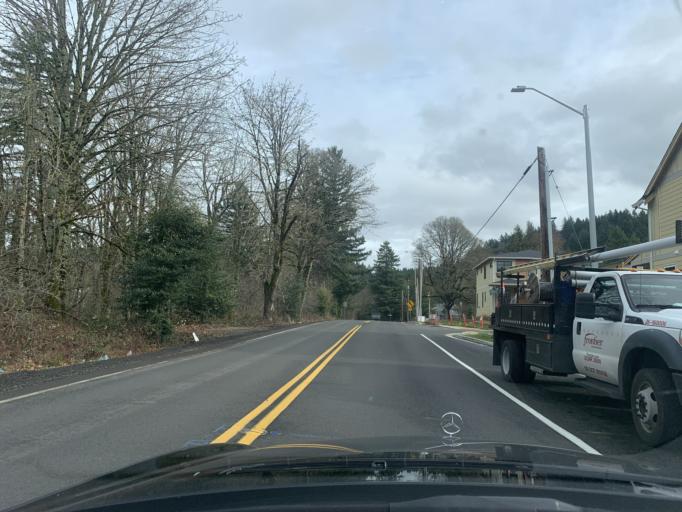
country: US
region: Oregon
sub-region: Multnomah County
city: Gresham
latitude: 45.4701
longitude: -122.4572
